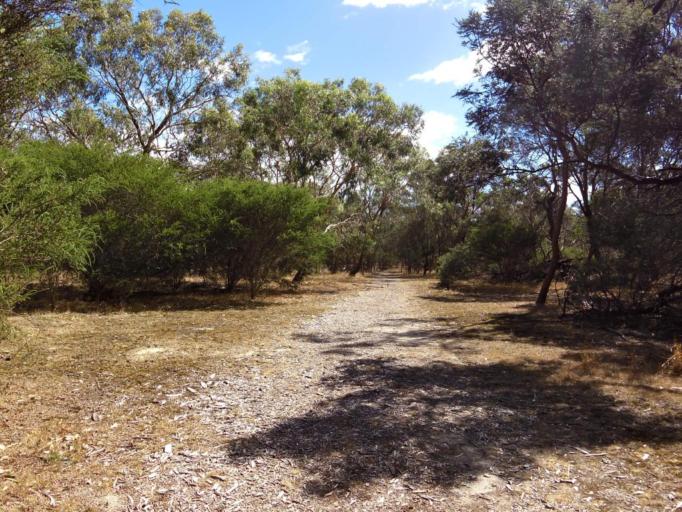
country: AU
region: Victoria
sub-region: Mornington Peninsula
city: Mount Martha
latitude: -38.2637
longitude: 145.0473
